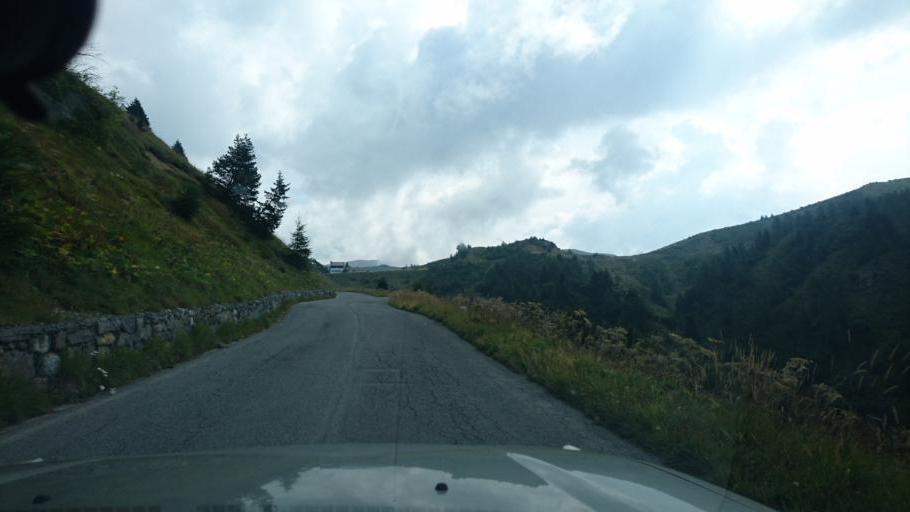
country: IT
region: Lombardy
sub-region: Provincia di Brescia
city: Prestine
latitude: 45.9079
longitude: 10.4046
